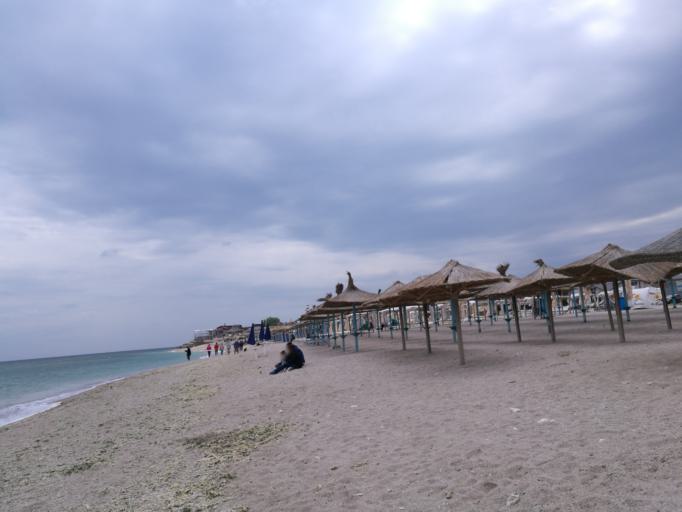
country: RO
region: Constanta
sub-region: Municipiul Mangalia
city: Mangalia
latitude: 43.7535
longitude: 28.5753
